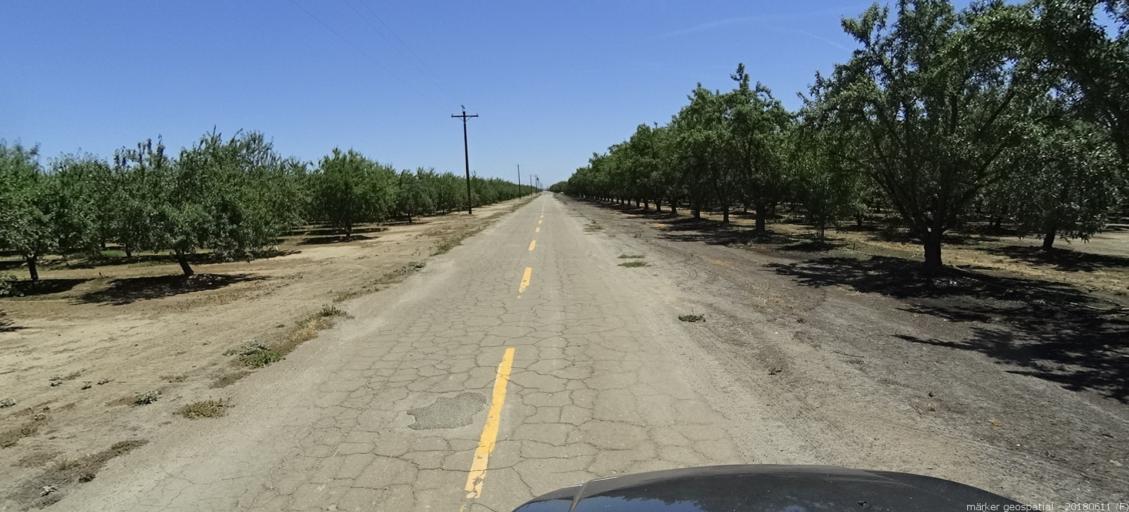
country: US
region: California
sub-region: Madera County
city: Fairmead
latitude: 37.0546
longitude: -120.2062
